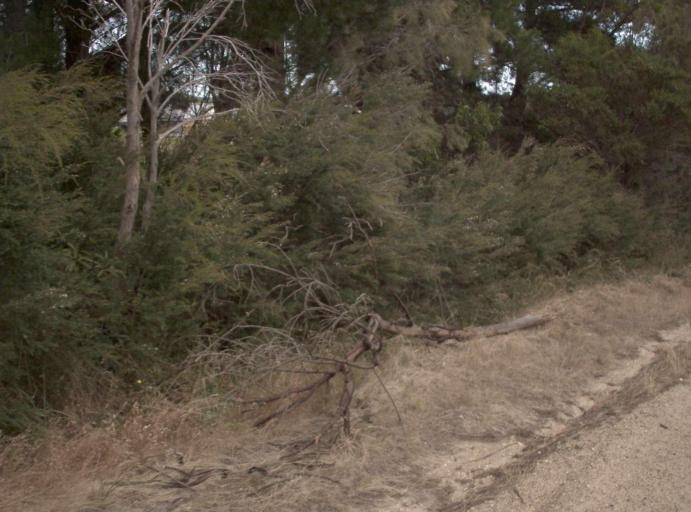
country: AU
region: Victoria
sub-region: Wellington
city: Sale
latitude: -38.1905
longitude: 147.0933
